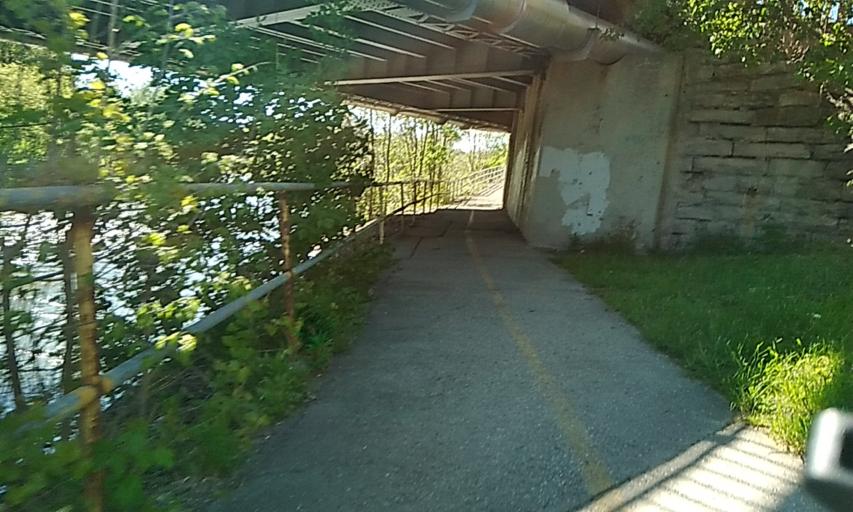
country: CA
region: Ontario
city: London
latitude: 42.9769
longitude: -81.2509
